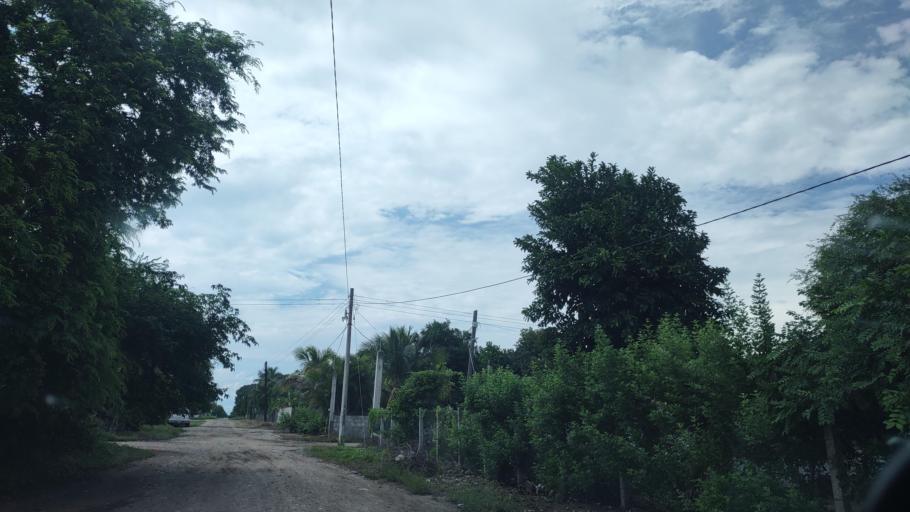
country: MX
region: Veracruz
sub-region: Panuco
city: Oviedo
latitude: 22.0022
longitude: -98.4544
